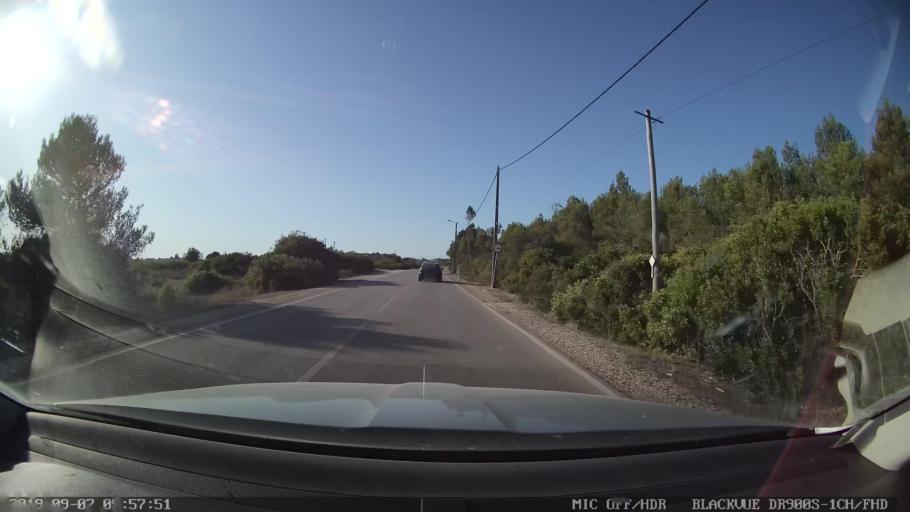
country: PT
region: Setubal
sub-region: Sesimbra
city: Sesimbra
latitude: 38.4546
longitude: -9.0919
